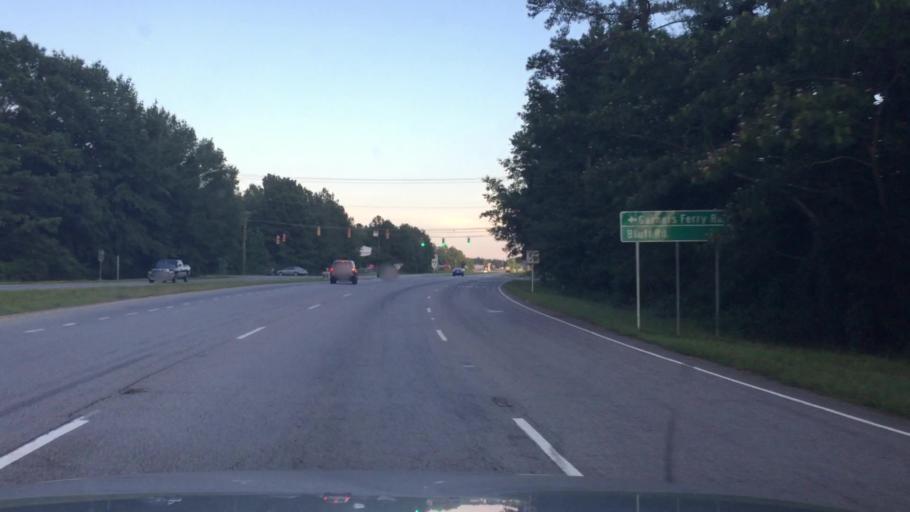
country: US
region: South Carolina
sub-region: Richland County
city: Forest Acres
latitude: 33.9490
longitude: -80.9663
